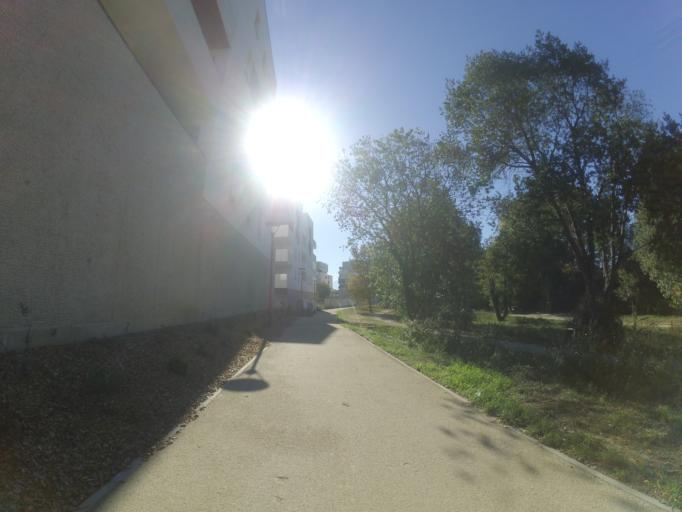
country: FR
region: Languedoc-Roussillon
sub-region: Departement des Pyrenees-Orientales
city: Perpignan
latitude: 42.6914
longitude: 2.8748
